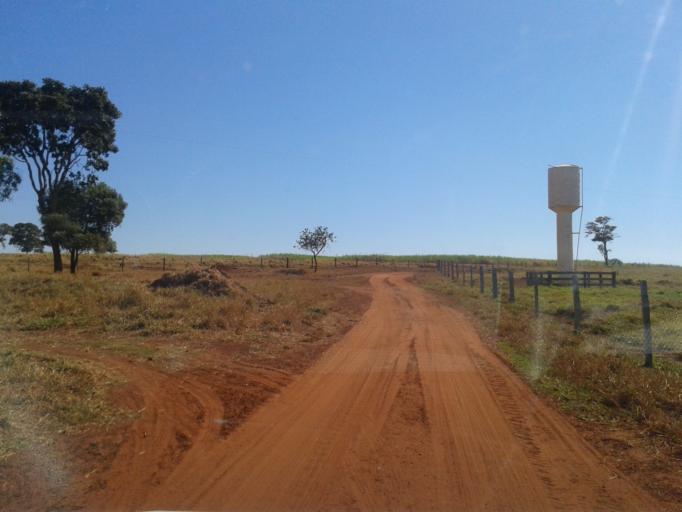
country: BR
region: Minas Gerais
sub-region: Santa Vitoria
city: Santa Vitoria
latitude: -19.1516
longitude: -50.2037
